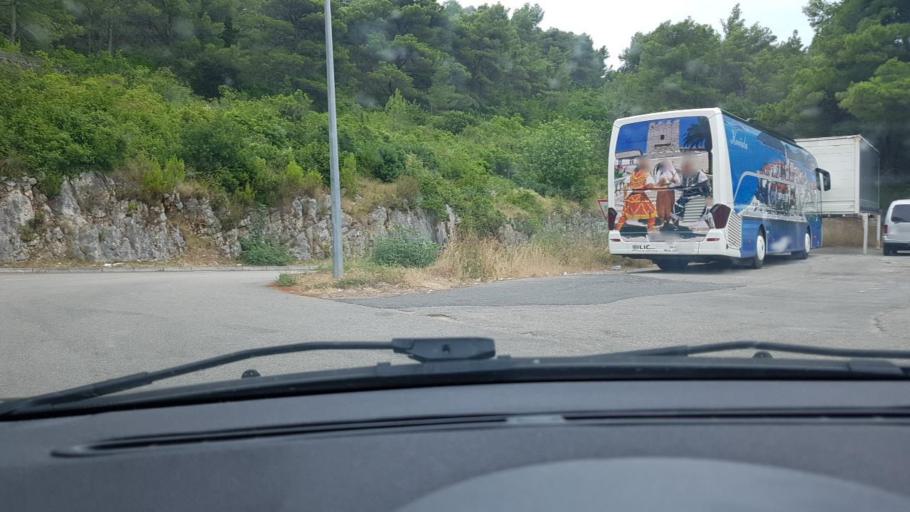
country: HR
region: Dubrovacko-Neretvanska
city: Korcula
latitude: 42.9593
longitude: 17.1279
